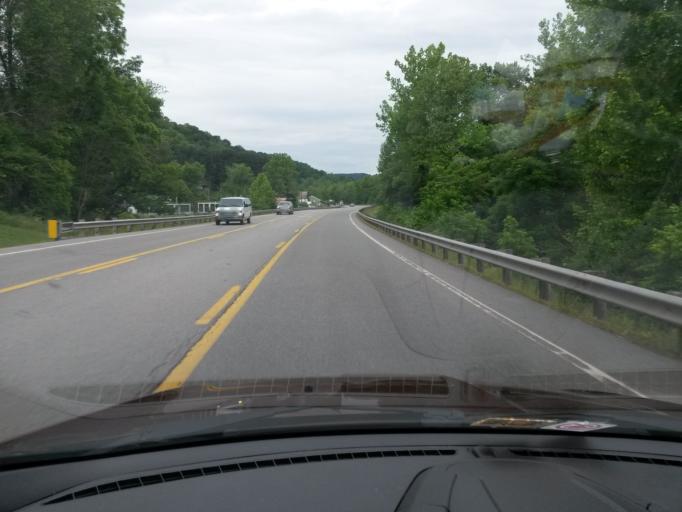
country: US
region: West Virginia
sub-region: Lewis County
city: Weston
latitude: 39.0307
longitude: -80.4364
